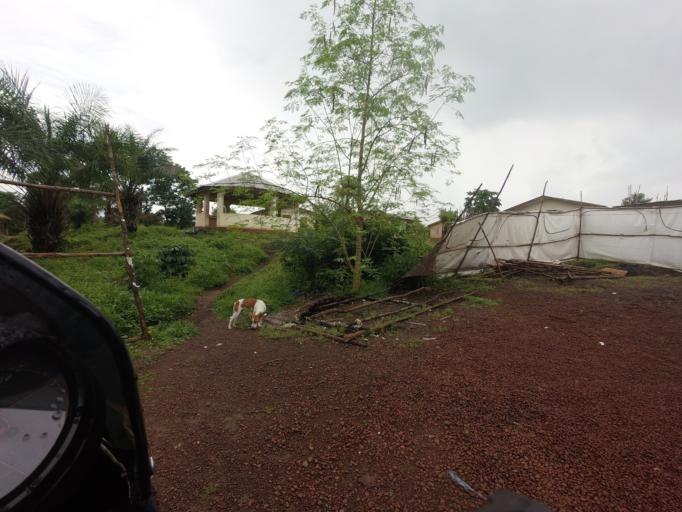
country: SL
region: Northern Province
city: Kambia
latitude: 9.1326
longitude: -12.9164
